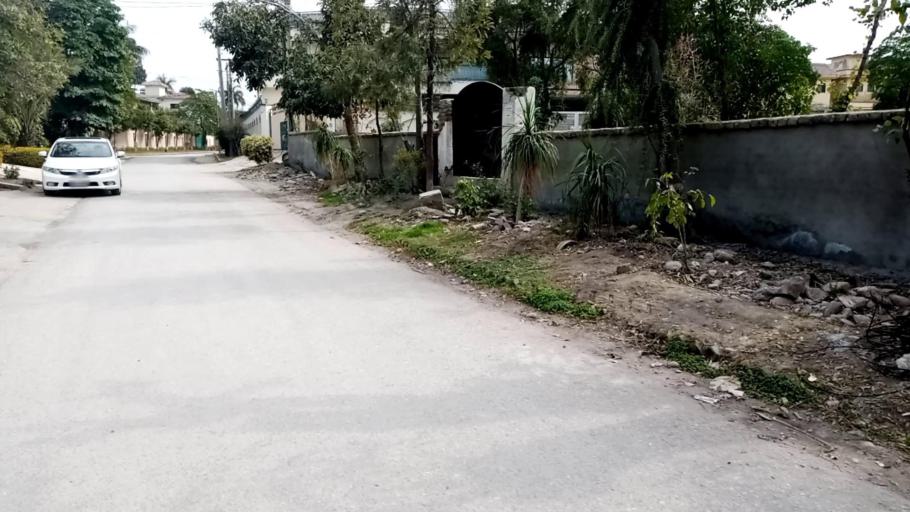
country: PK
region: Khyber Pakhtunkhwa
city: Peshawar
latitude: 33.9643
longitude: 71.4326
